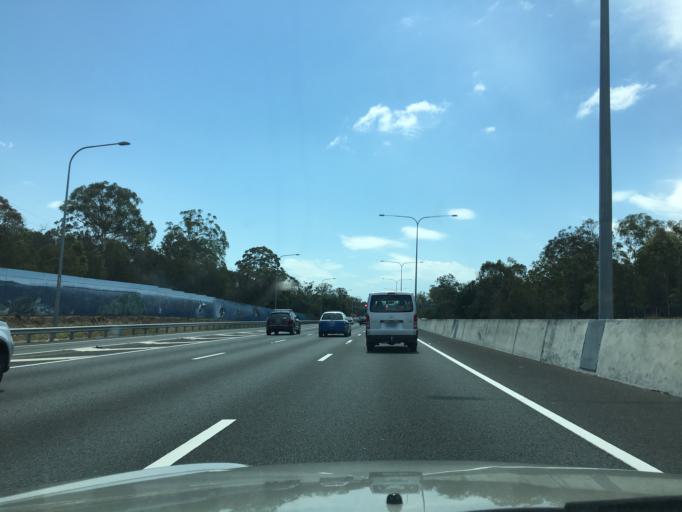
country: AU
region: Queensland
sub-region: Brisbane
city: Upper Mount Gravatt
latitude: -27.5740
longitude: 153.1067
